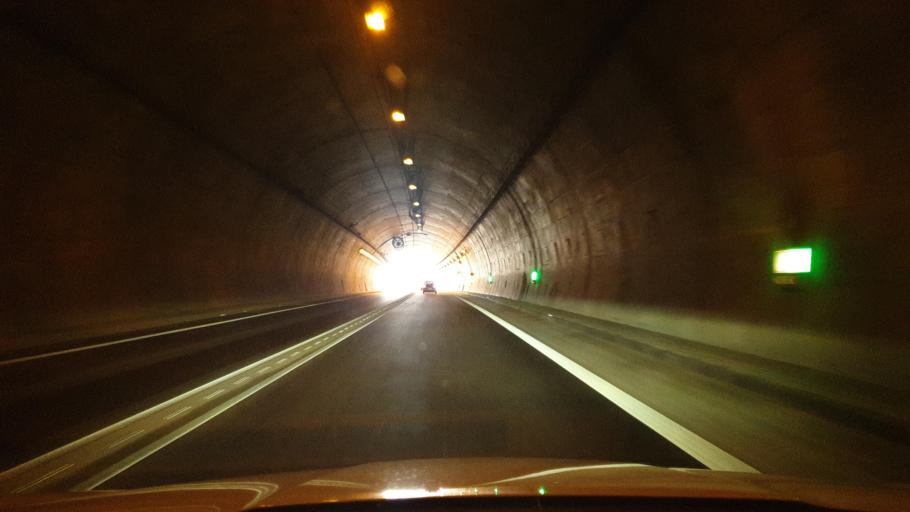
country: DE
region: North Rhine-Westphalia
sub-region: Regierungsbezirk Detmold
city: Oerlinghausen
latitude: 51.9556
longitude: 8.6502
